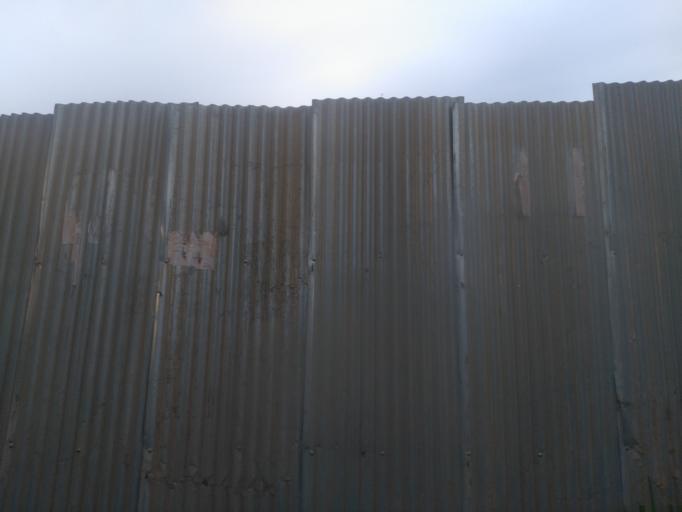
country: UG
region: Central Region
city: Kampala Central Division
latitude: 0.3440
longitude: 32.5794
